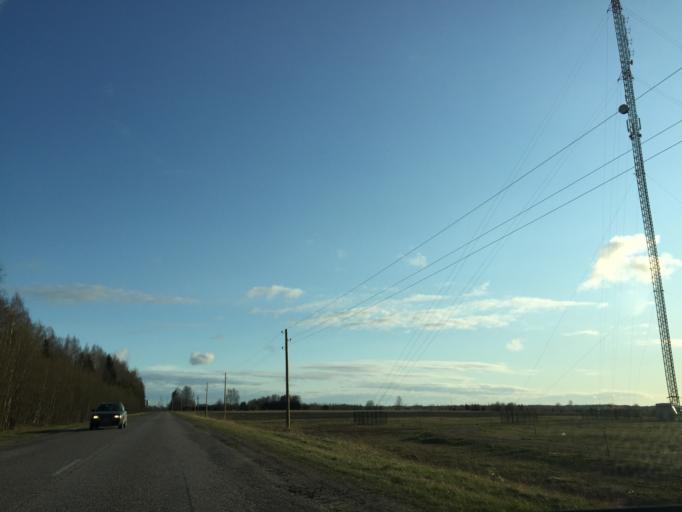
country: LV
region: Limbazu Rajons
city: Limbazi
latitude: 57.5329
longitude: 24.7401
